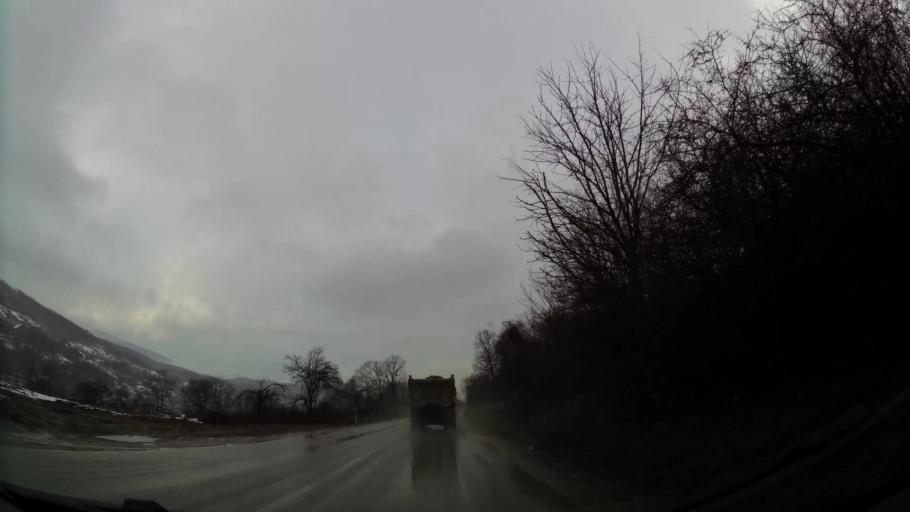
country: XK
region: Ferizaj
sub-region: Komuna e Kacanikut
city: Kacanik
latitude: 42.2353
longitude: 21.2490
